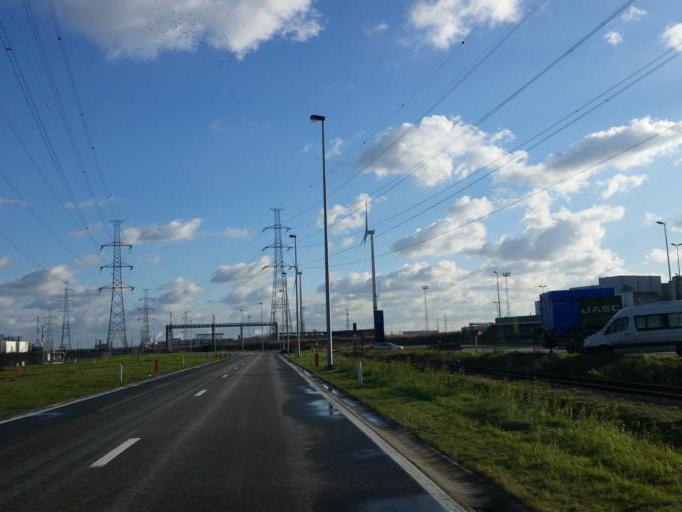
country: BE
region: Flanders
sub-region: Provincie Oost-Vlaanderen
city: Beveren
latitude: 51.2916
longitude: 4.2707
